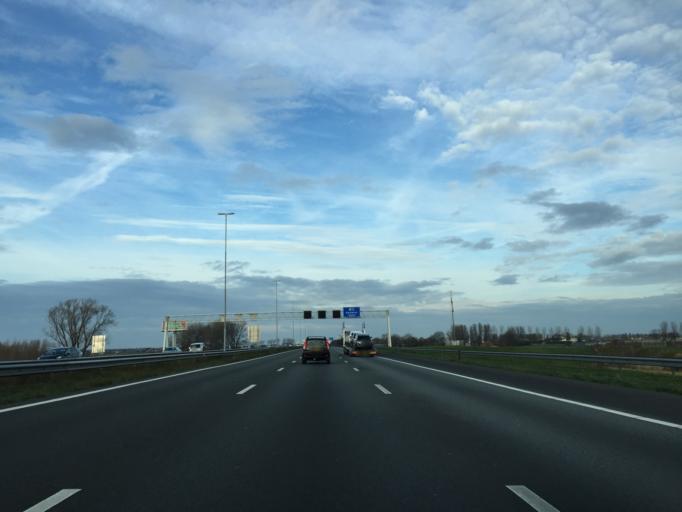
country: NL
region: Gelderland
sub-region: Gemeente Maasdriel
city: Hedel
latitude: 51.7456
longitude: 5.2972
